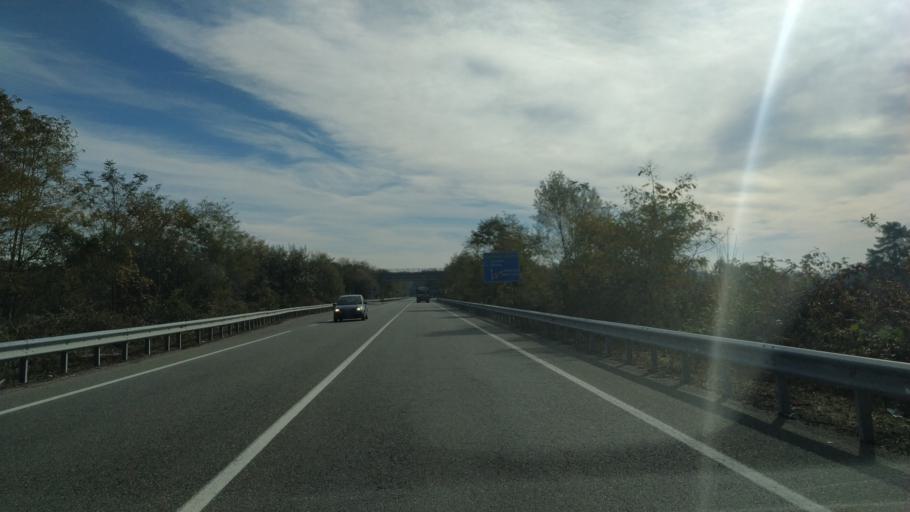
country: IT
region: Piedmont
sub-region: Provincia di Novara
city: Prato Sesia
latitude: 45.6656
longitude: 8.3638
